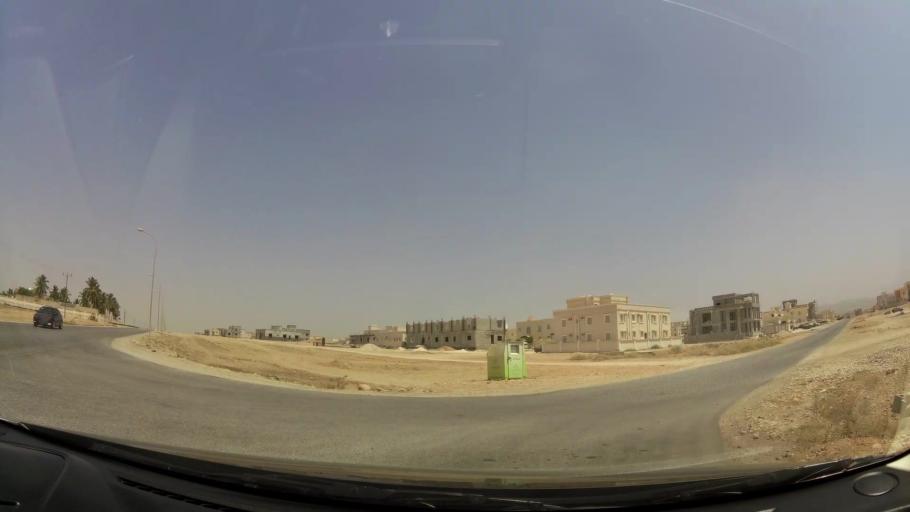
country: OM
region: Zufar
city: Salalah
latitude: 17.0686
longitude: 54.2001
